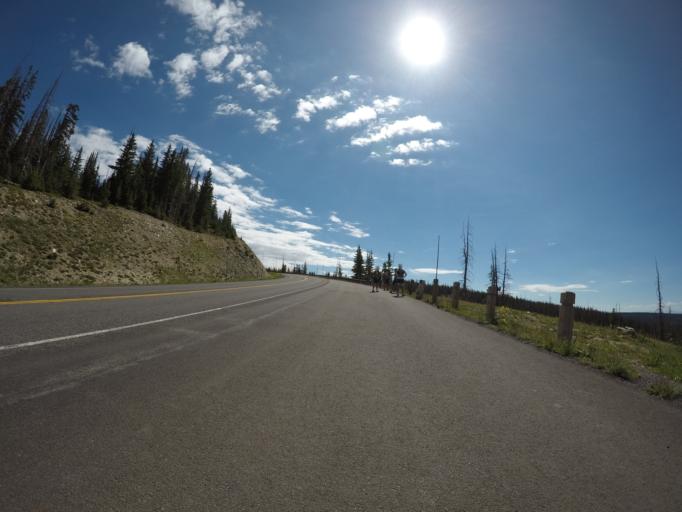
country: US
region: Wyoming
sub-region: Carbon County
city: Saratoga
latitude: 41.3127
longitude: -106.3570
